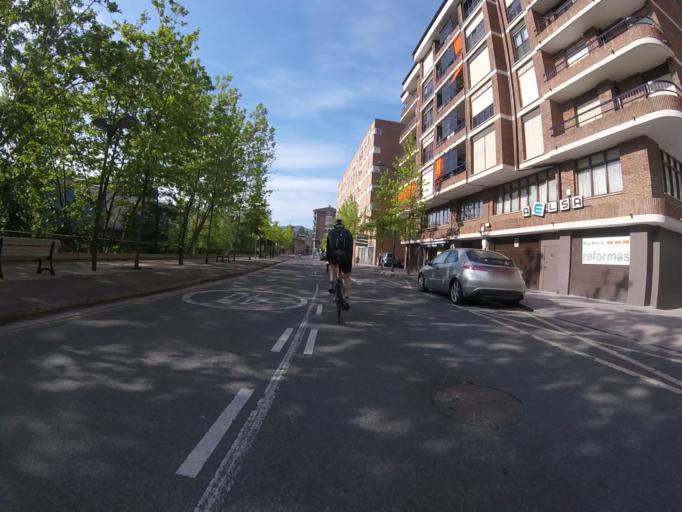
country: ES
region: Basque Country
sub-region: Provincia de Guipuzcoa
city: Beasain
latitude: 43.0523
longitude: -2.1898
